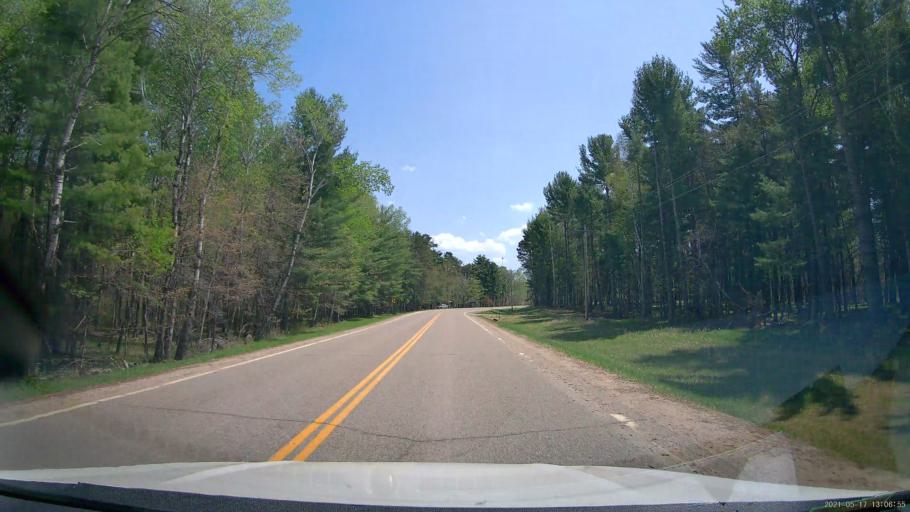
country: US
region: Minnesota
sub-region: Hubbard County
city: Park Rapids
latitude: 47.0512
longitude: -94.9189
